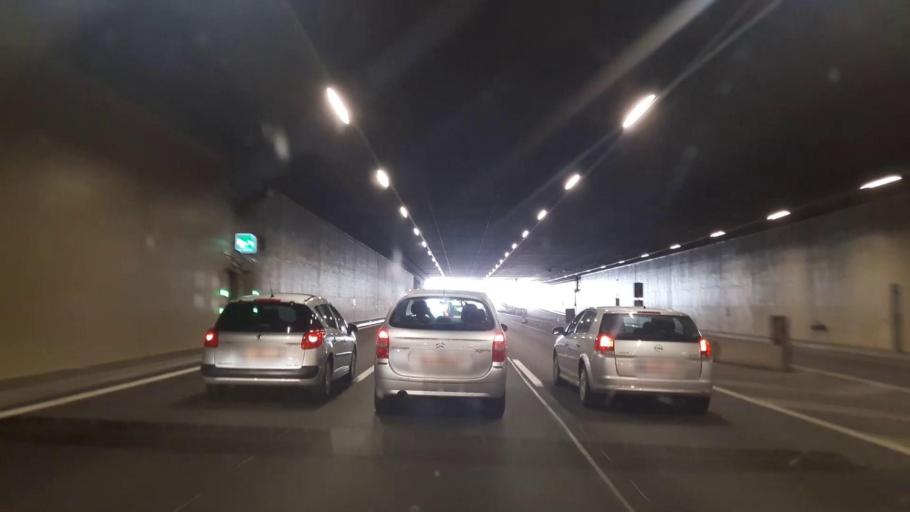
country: AT
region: Vienna
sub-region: Wien Stadt
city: Vienna
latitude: 48.2220
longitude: 16.4243
